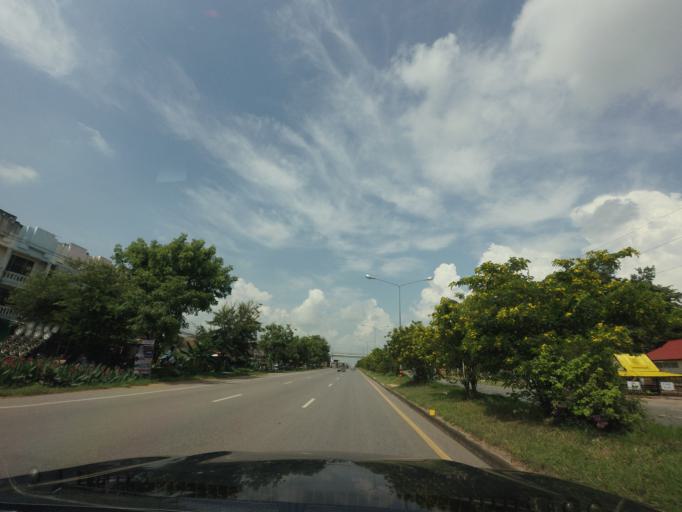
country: TH
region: Khon Kaen
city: Ban Fang
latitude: 16.4502
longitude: 102.7257
